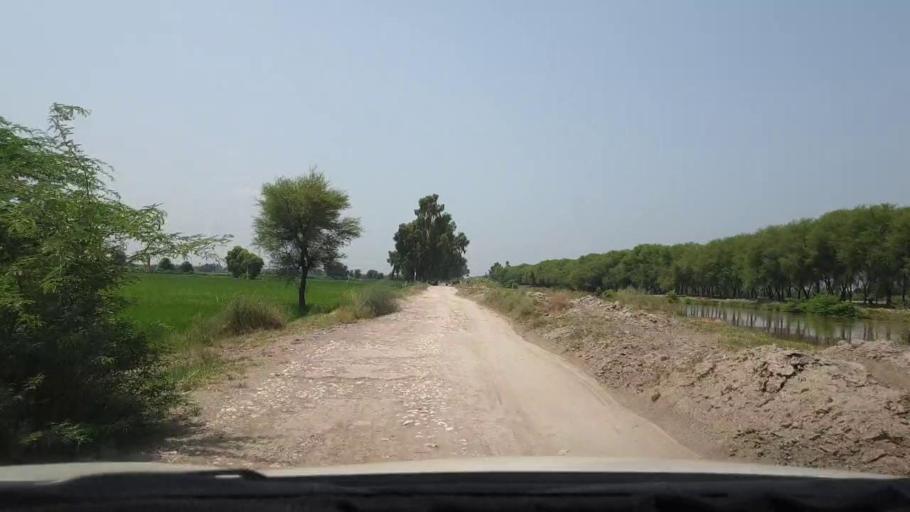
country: PK
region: Sindh
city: Dokri
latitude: 27.3073
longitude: 68.0964
